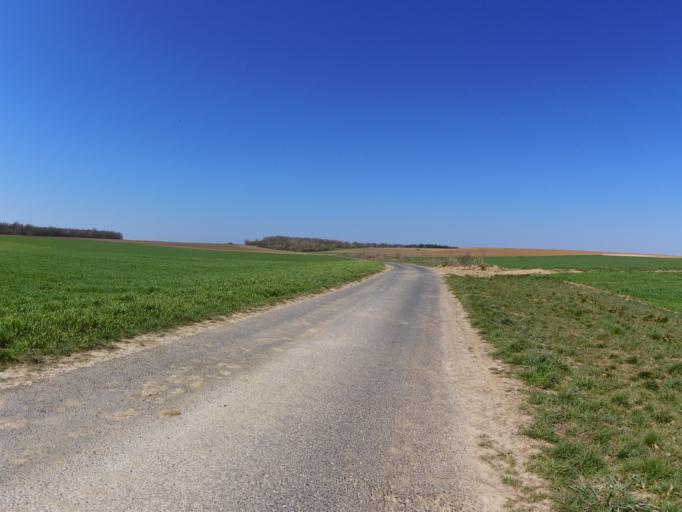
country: DE
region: Bavaria
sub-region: Regierungsbezirk Unterfranken
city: Oberpleichfeld
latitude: 49.8339
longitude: 10.0835
